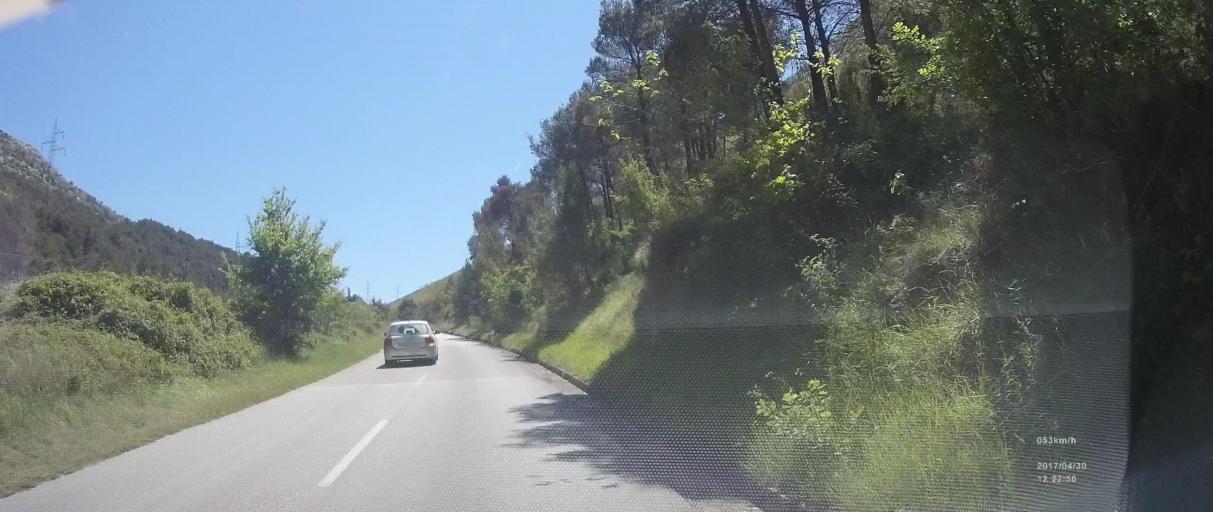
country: HR
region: Splitsko-Dalmatinska
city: Zrnovnica
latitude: 43.5186
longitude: 16.5742
